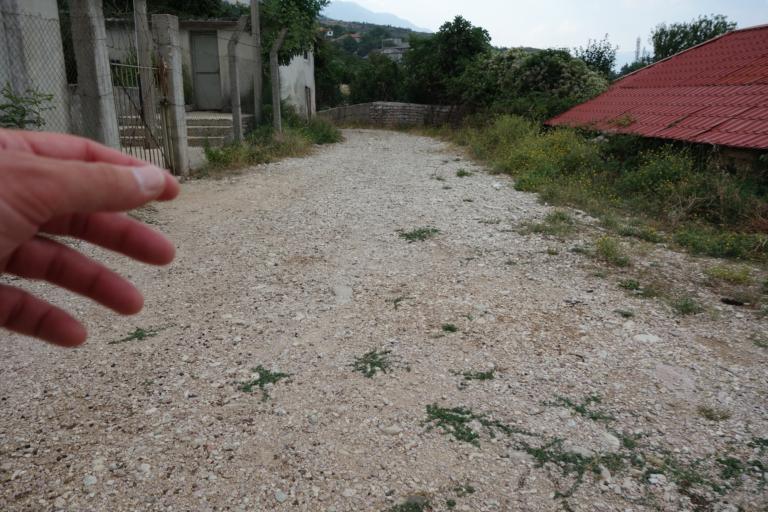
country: AL
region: Gjirokaster
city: Gjirokaster
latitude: 40.0680
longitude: 20.1349
